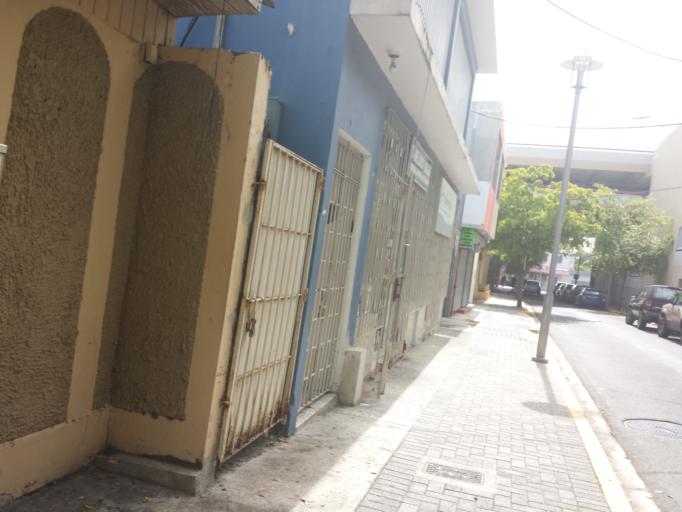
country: PR
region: Carolina
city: Carolina
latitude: 18.3819
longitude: -65.9566
